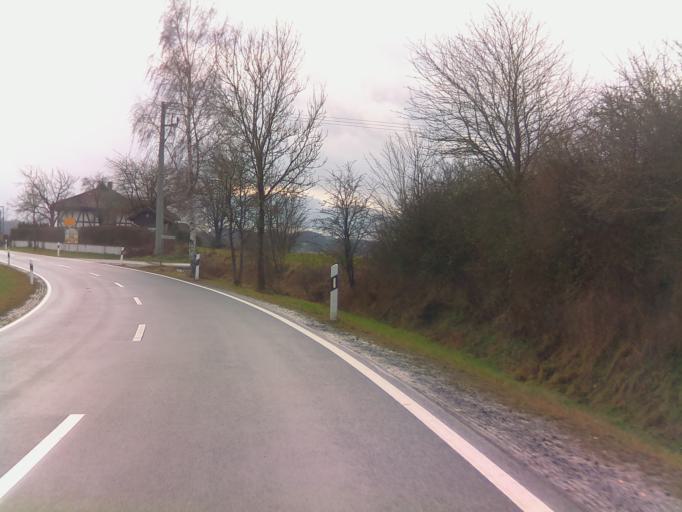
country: DE
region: Hesse
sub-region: Regierungsbezirk Kassel
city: Flieden
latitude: 50.4124
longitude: 9.5829
